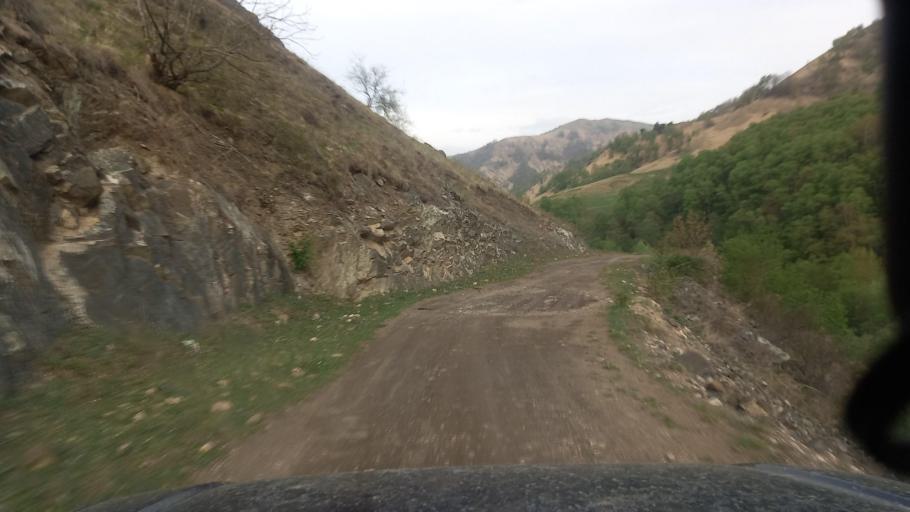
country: RU
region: Kabardino-Balkariya
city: Kamennomostskoye
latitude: 43.7212
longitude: 42.8652
